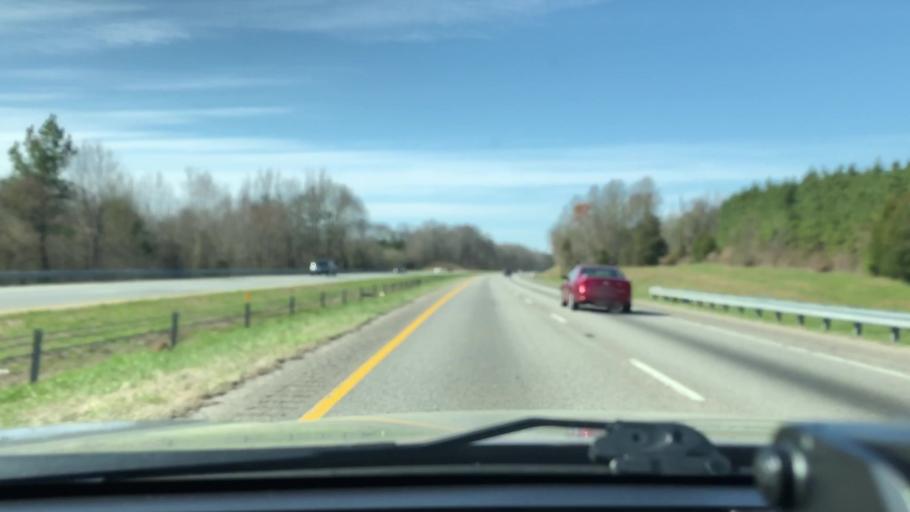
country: US
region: South Carolina
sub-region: Spartanburg County
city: Roebuck
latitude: 34.8652
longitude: -81.9849
